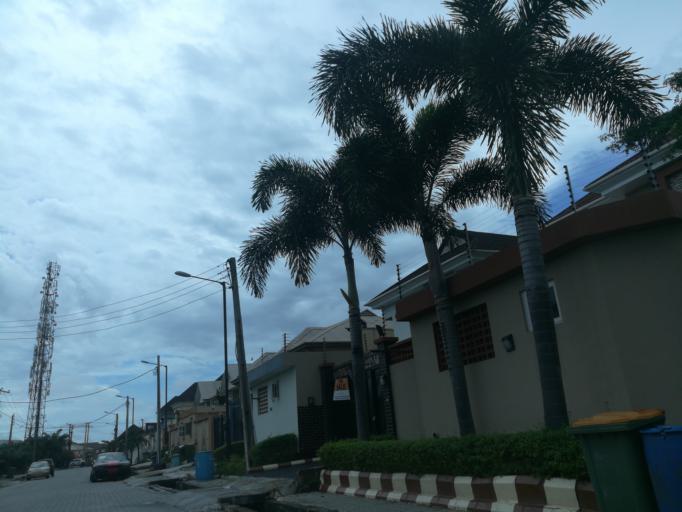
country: NG
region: Lagos
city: Ikoyi
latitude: 6.4379
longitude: 3.4759
